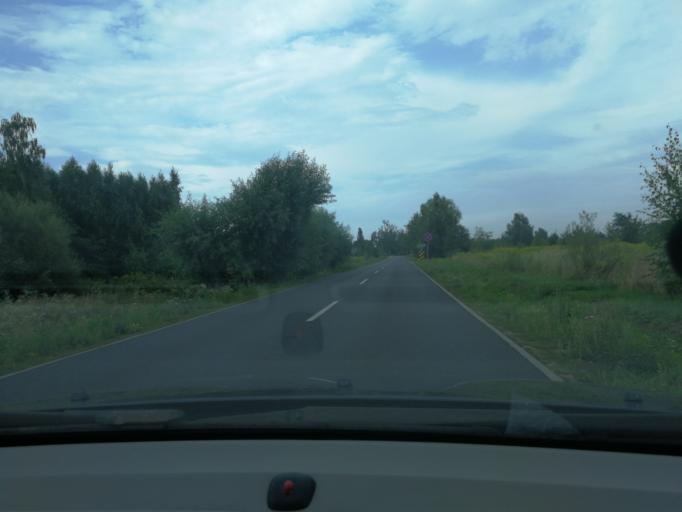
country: PL
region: Masovian Voivodeship
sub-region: Powiat grodziski
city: Grodzisk Mazowiecki
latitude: 52.1441
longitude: 20.6343
